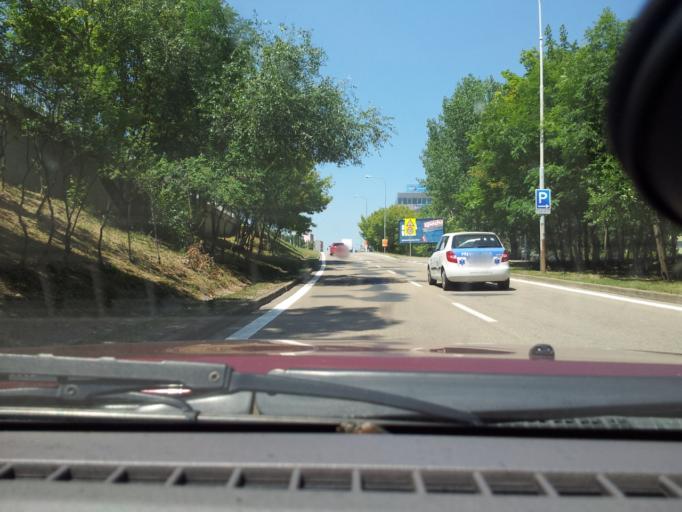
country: CZ
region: South Moravian
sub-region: Mesto Brno
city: Brno
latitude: 49.1693
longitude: 16.5984
